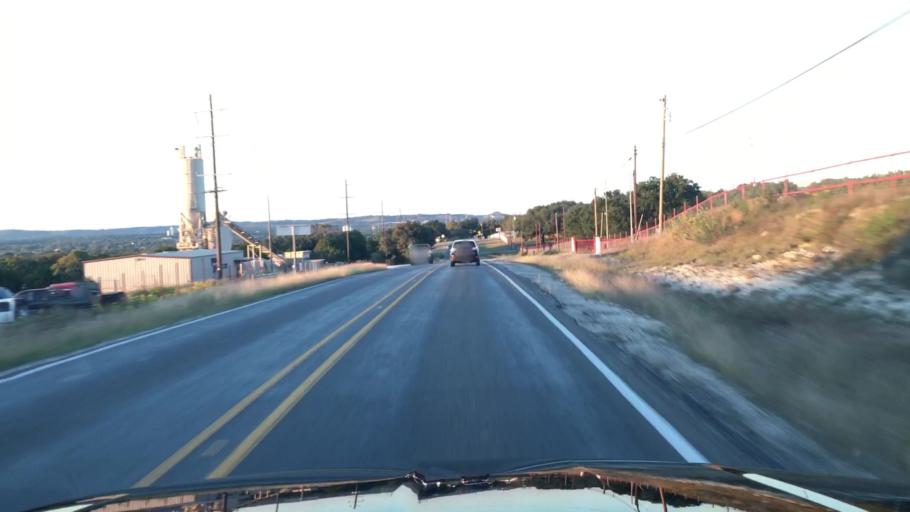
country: US
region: Texas
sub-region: Blanco County
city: Blanco
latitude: 30.0771
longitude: -98.4121
